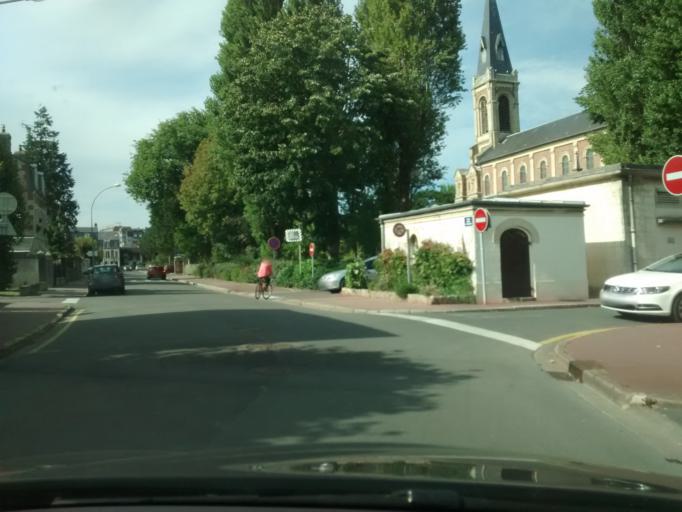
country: FR
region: Lower Normandy
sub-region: Departement du Calvados
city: Deauville
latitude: 49.3539
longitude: 0.0707
